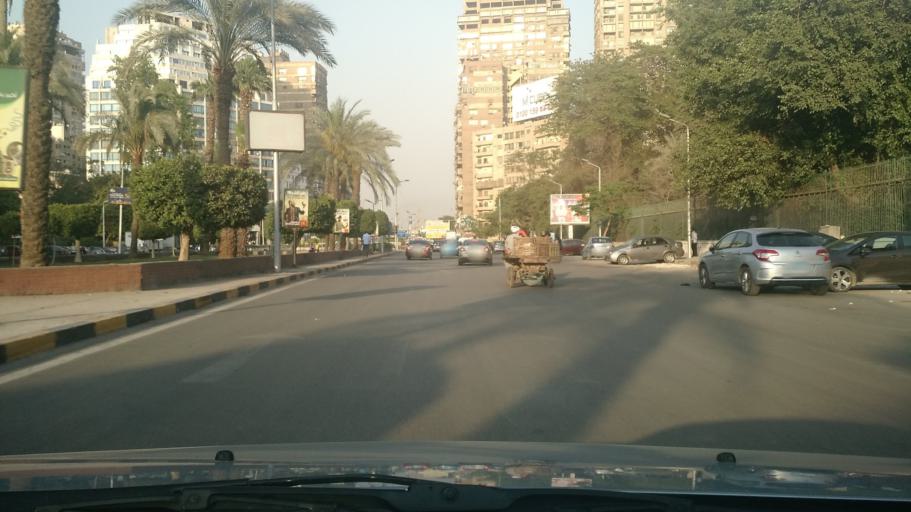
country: EG
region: Al Jizah
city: Al Jizah
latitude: 30.0279
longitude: 31.2141
